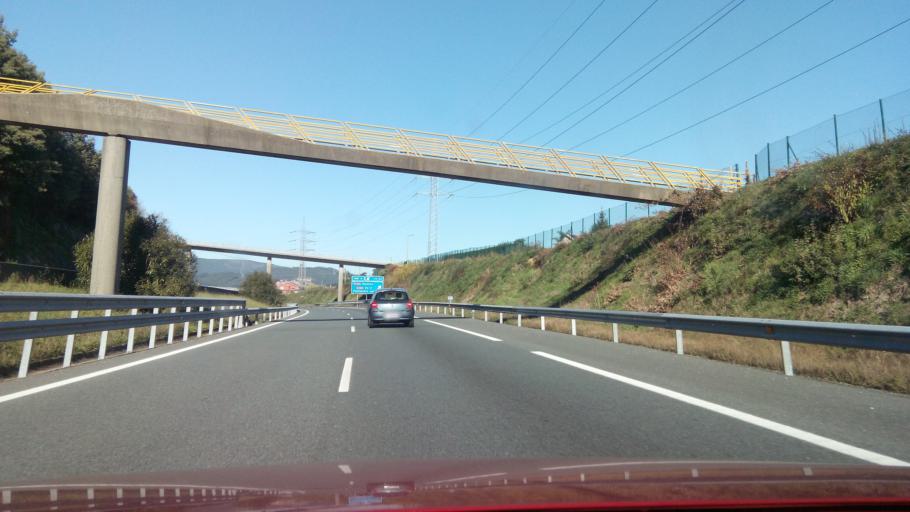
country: ES
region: Galicia
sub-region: Provincia de Pontevedra
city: Pontevedra
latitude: 42.4007
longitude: -8.6490
